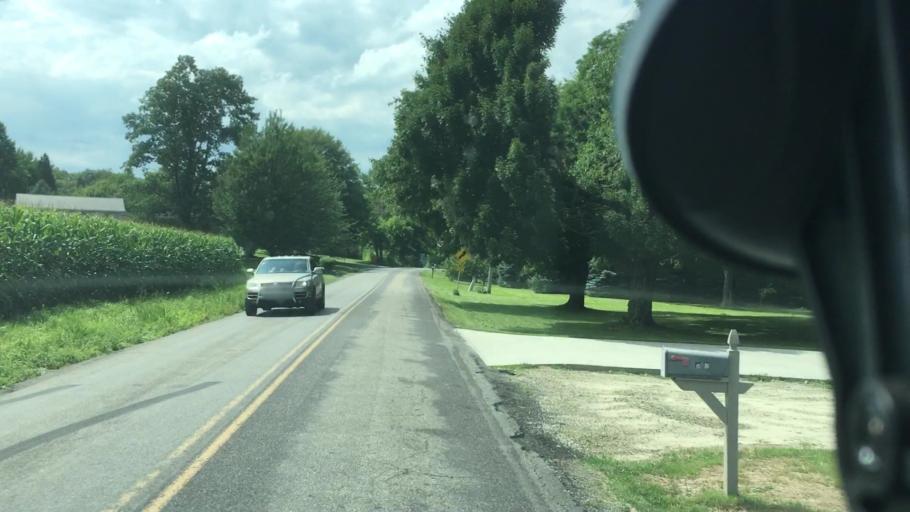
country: US
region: Pennsylvania
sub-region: Mercer County
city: Reynolds Heights
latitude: 41.3013
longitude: -80.3647
